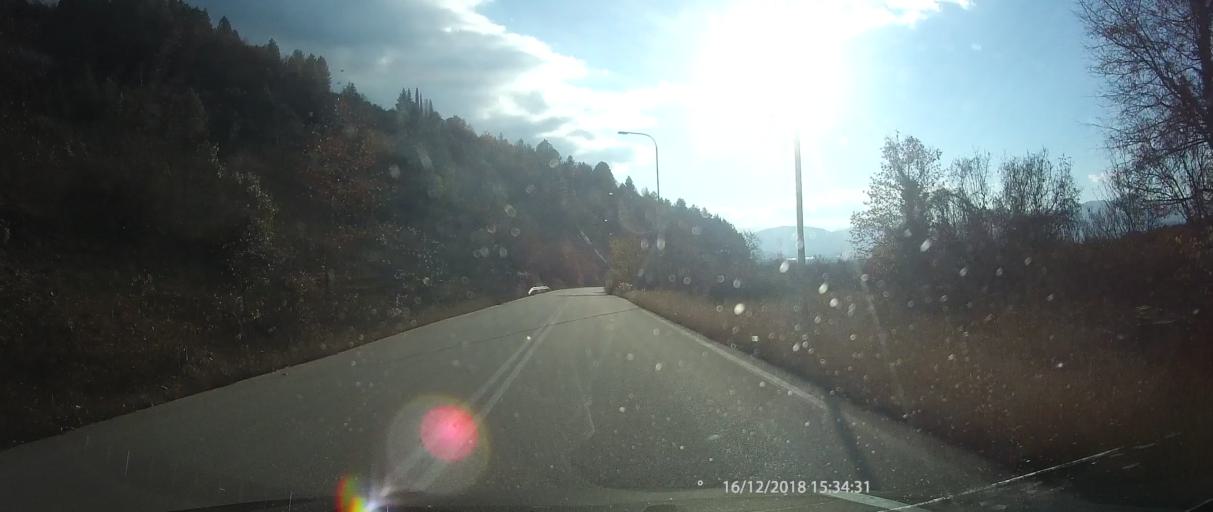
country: GR
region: Epirus
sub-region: Nomos Ioanninon
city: Konitsa
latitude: 40.0606
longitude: 20.7412
